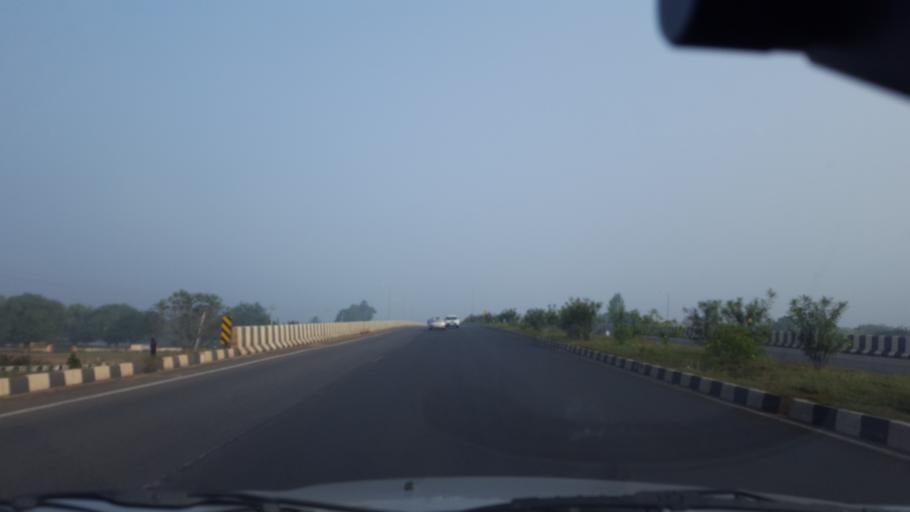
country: IN
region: Andhra Pradesh
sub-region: Prakasam
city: Ongole
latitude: 15.3882
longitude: 80.0393
